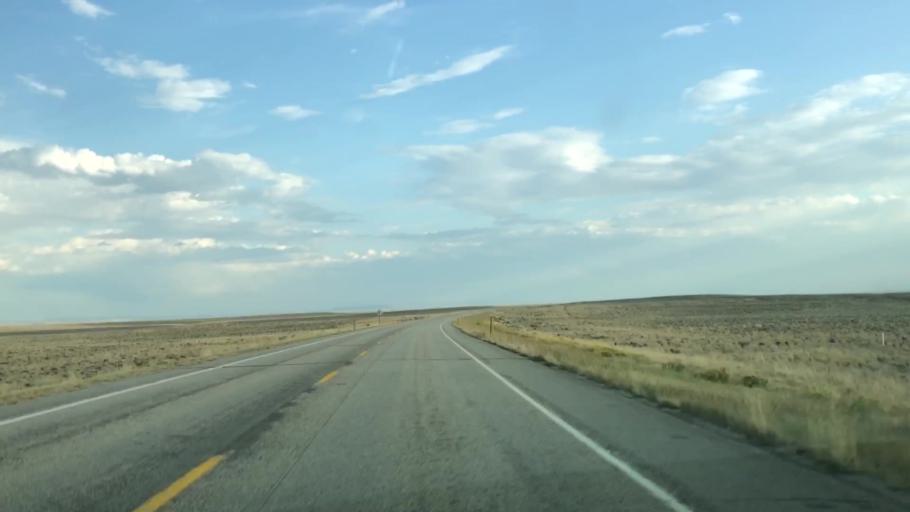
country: US
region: Wyoming
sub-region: Sweetwater County
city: North Rock Springs
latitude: 42.2568
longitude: -109.4695
